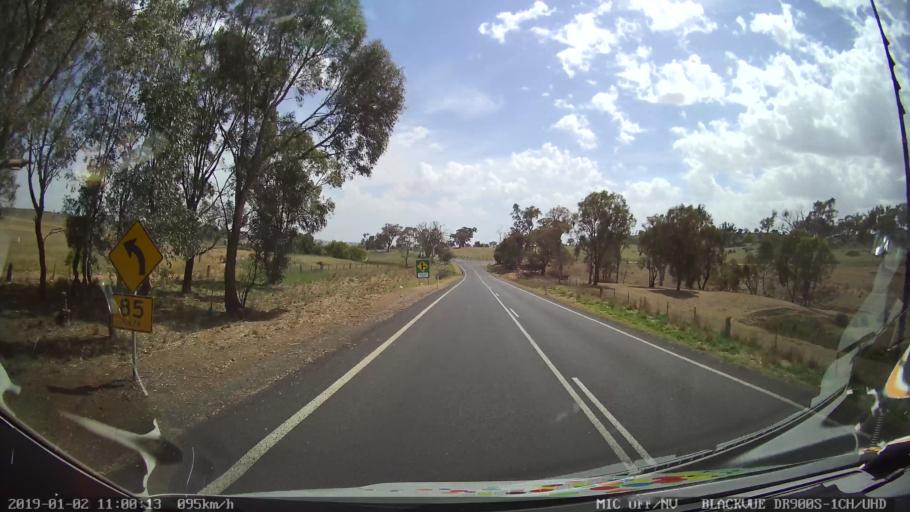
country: AU
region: New South Wales
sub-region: Cootamundra
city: Cootamundra
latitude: -34.6069
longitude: 148.3127
